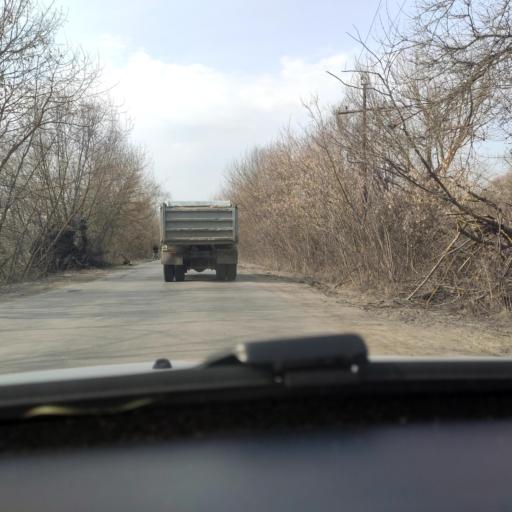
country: RU
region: Voronezj
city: Ramon'
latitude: 51.9073
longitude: 39.3571
